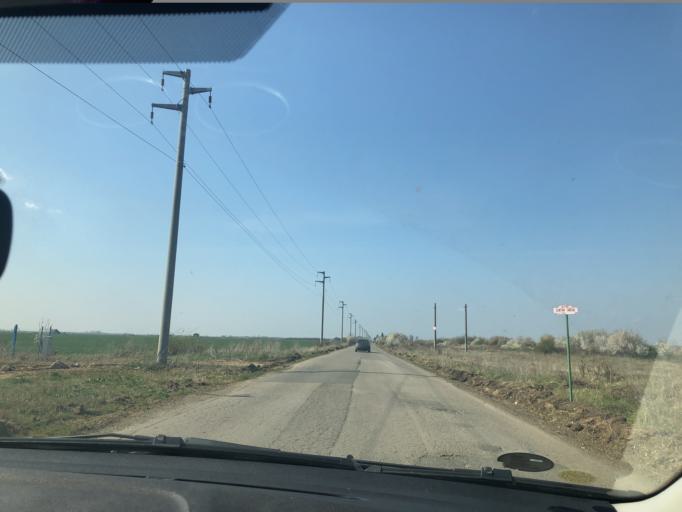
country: RO
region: Ilfov
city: Domnesti-Sarbi
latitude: 44.3729
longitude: 25.9273
